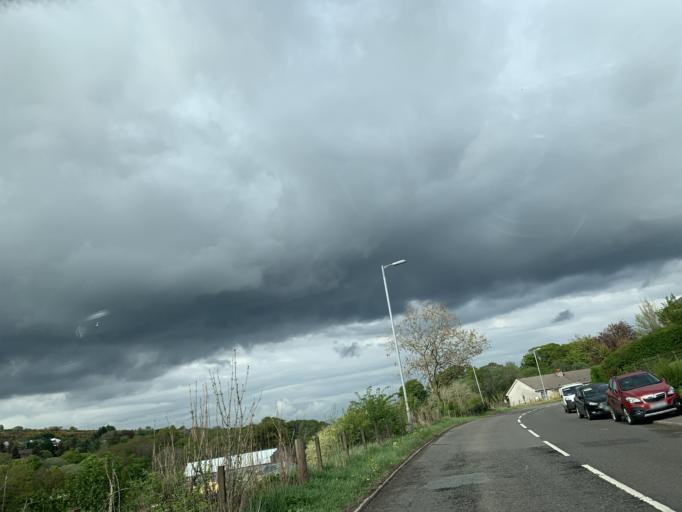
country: GB
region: Scotland
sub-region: East Renfrewshire
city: Barrhead
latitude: 55.7955
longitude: -4.4090
